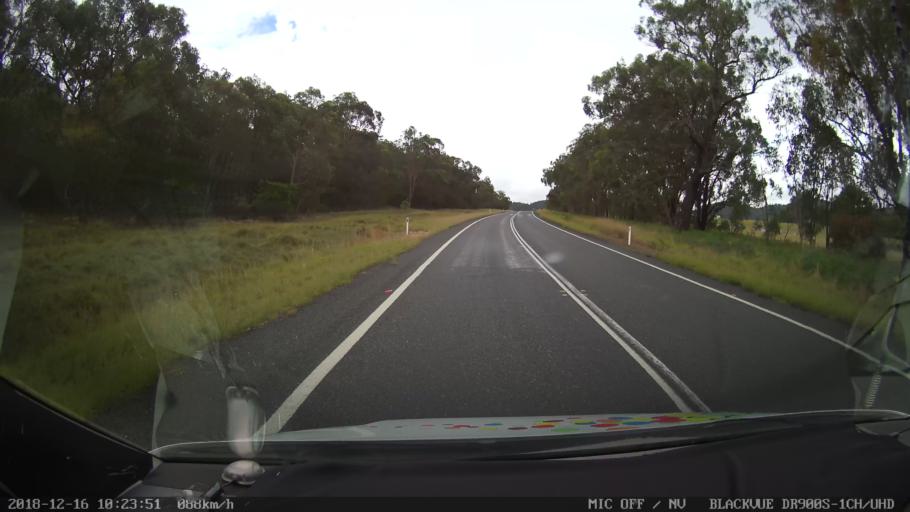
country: AU
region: New South Wales
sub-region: Tenterfield Municipality
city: Carrolls Creek
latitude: -29.1775
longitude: 152.0051
